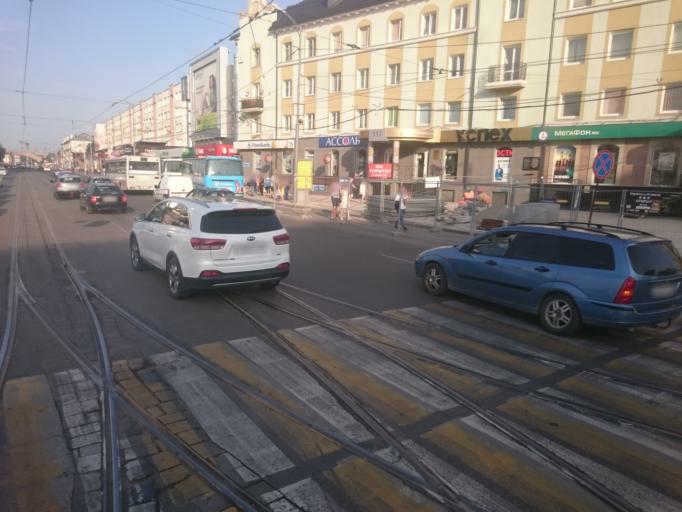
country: RU
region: Kaliningrad
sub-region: Gorod Kaliningrad
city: Kaliningrad
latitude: 54.7188
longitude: 20.5021
